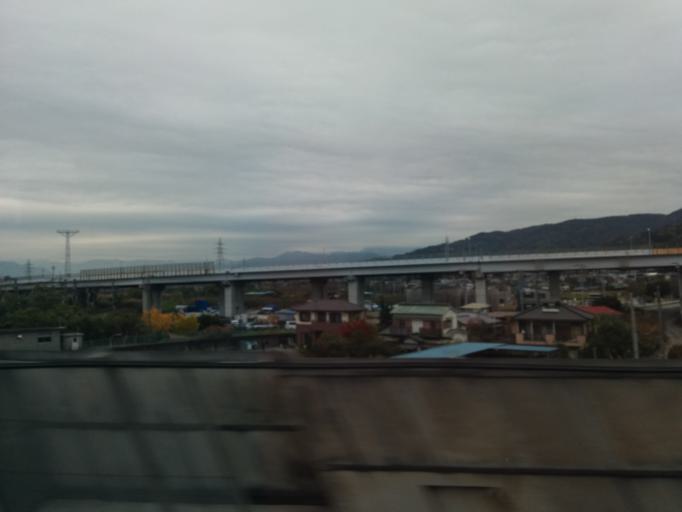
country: JP
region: Kanagawa
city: Odawara
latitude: 35.2890
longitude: 139.2007
